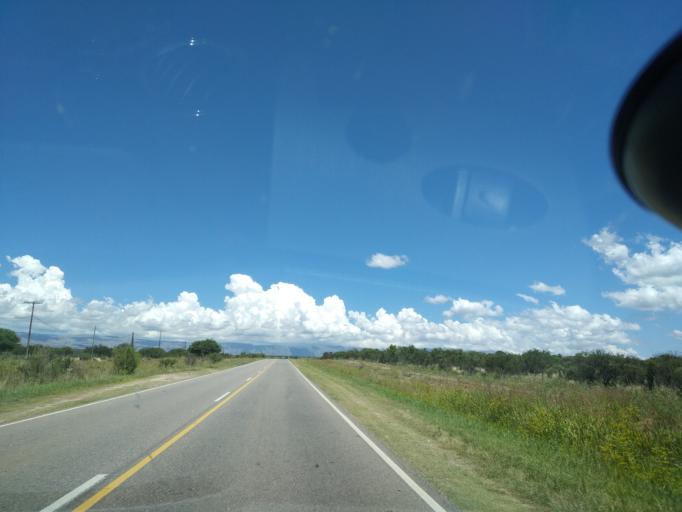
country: AR
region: Cordoba
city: Villa Cura Brochero
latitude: -31.6758
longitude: -65.0886
